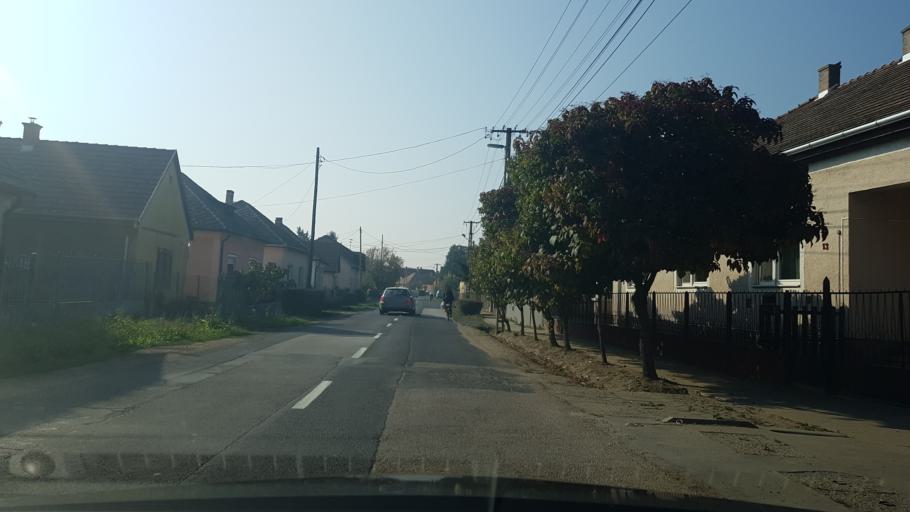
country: HU
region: Fejer
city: Adony
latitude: 47.1186
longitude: 18.8643
